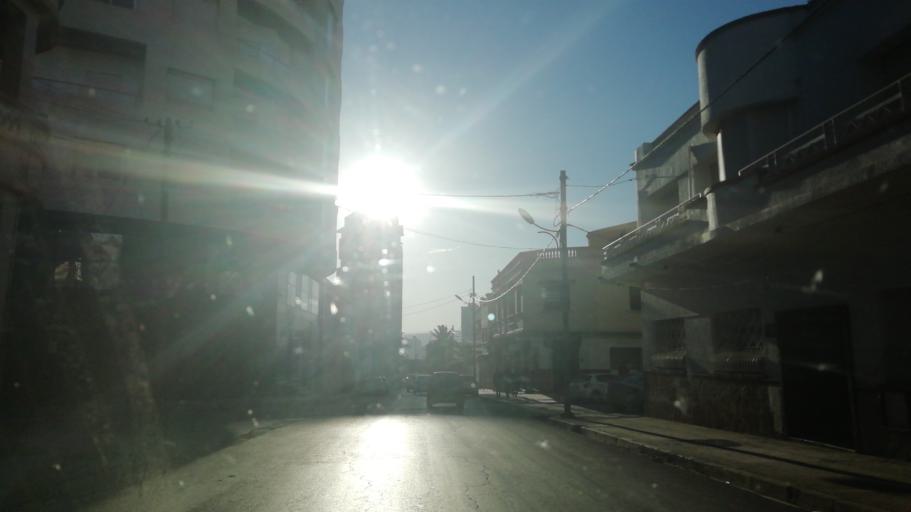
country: DZ
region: Oran
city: Oran
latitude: 35.7121
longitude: -0.6183
